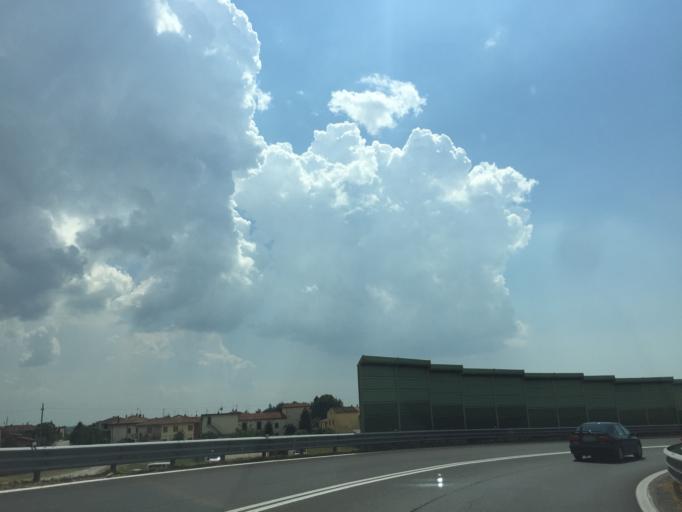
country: IT
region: Tuscany
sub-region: Provincia di Pistoia
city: Pieve a Nievole
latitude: 43.8759
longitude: 10.7944
